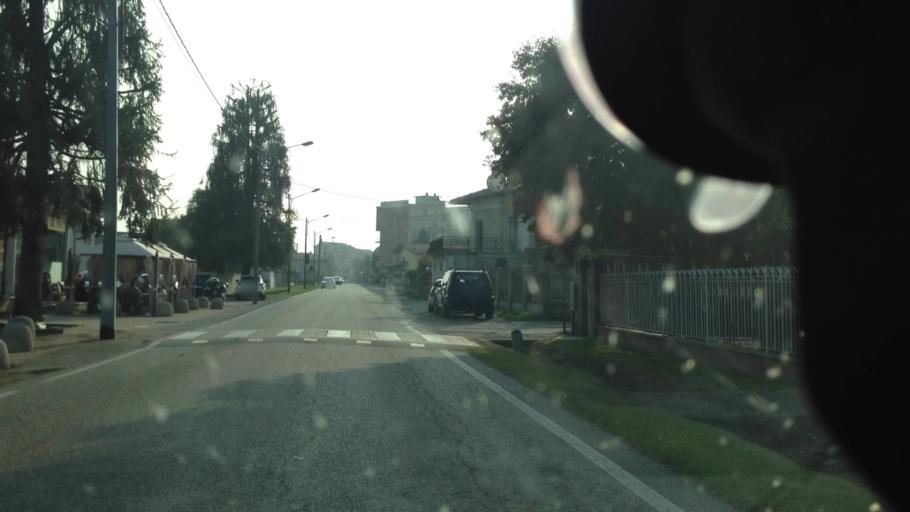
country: IT
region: Piedmont
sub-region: Provincia di Vercelli
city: Cigliano
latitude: 45.3142
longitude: 8.0273
